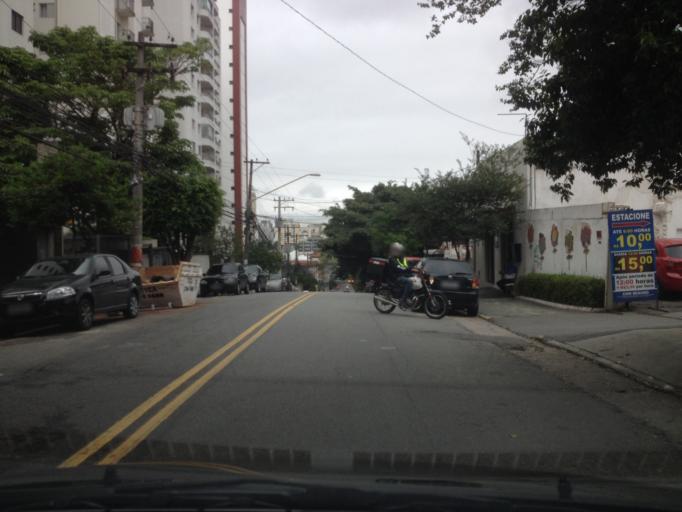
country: BR
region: Sao Paulo
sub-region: Sao Paulo
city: Sao Paulo
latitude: -23.5541
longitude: -46.6901
